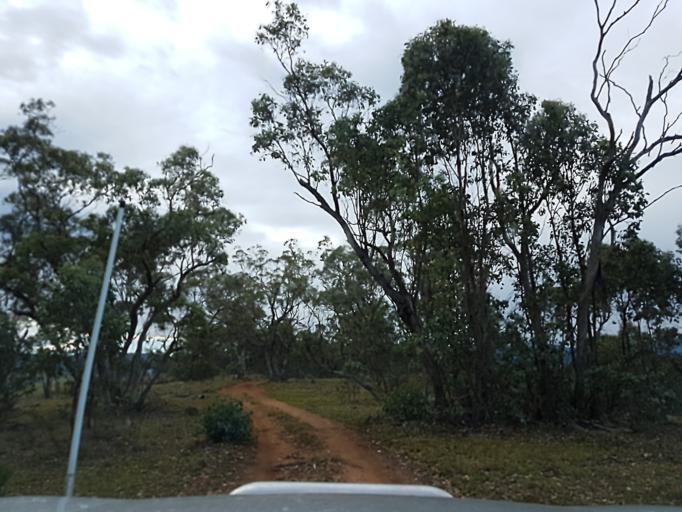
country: AU
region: New South Wales
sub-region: Snowy River
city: Jindabyne
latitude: -36.9633
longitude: 148.3816
